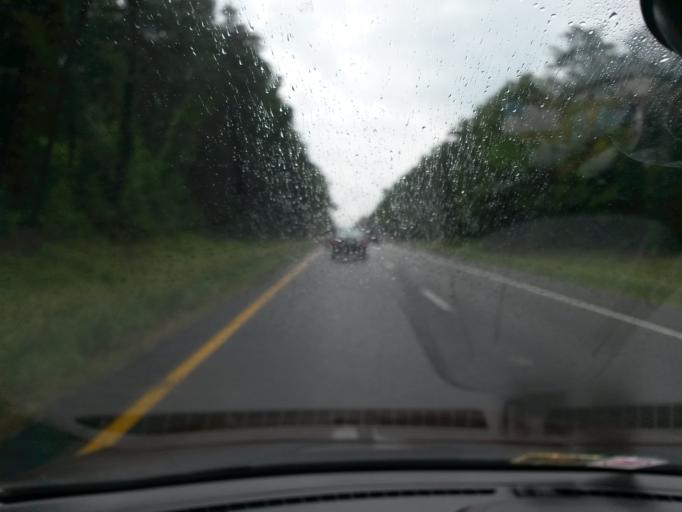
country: US
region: Virginia
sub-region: Goochland County
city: Goochland
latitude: 37.7684
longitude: -77.8735
